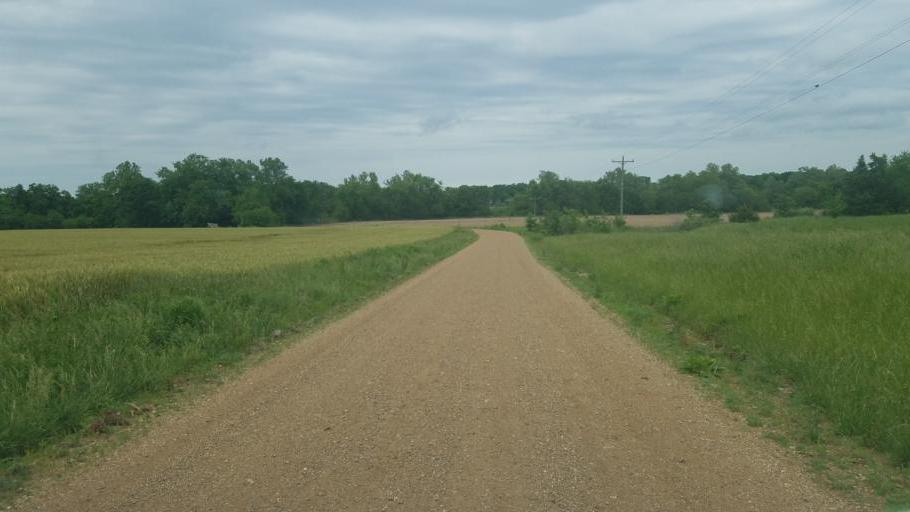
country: US
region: Missouri
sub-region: Moniteau County
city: Tipton
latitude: 38.5534
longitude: -92.7279
